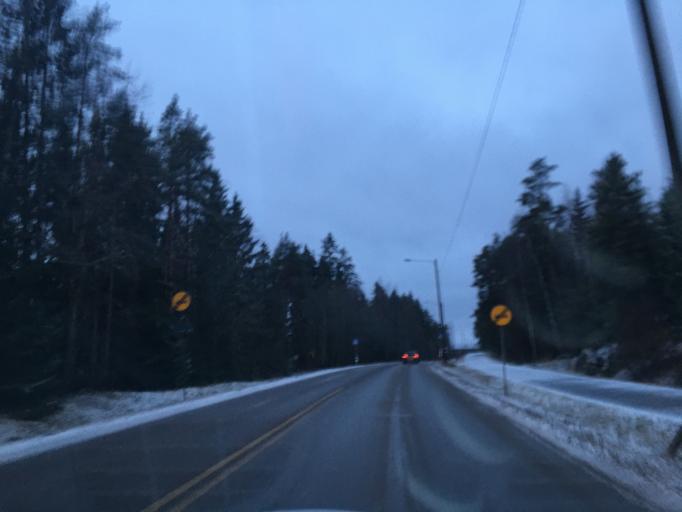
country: FI
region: Varsinais-Suomi
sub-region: Loimaa
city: Aura
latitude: 60.6449
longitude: 22.6045
